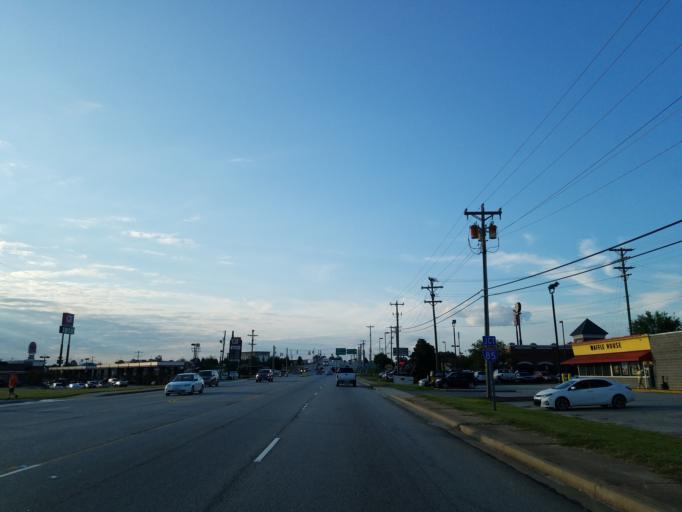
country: US
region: South Carolina
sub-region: Cherokee County
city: Gaffney
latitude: 35.0791
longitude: -81.7032
